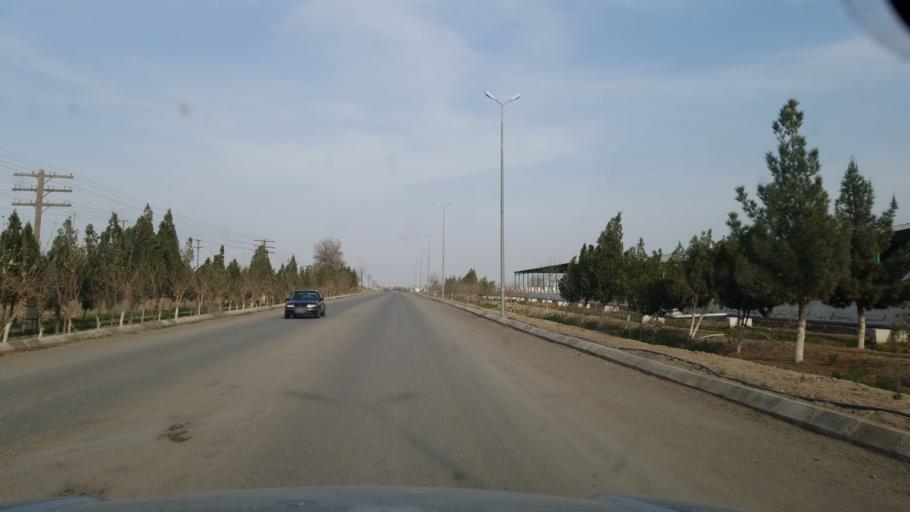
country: TM
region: Mary
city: Bayramaly
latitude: 37.6249
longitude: 62.1749
